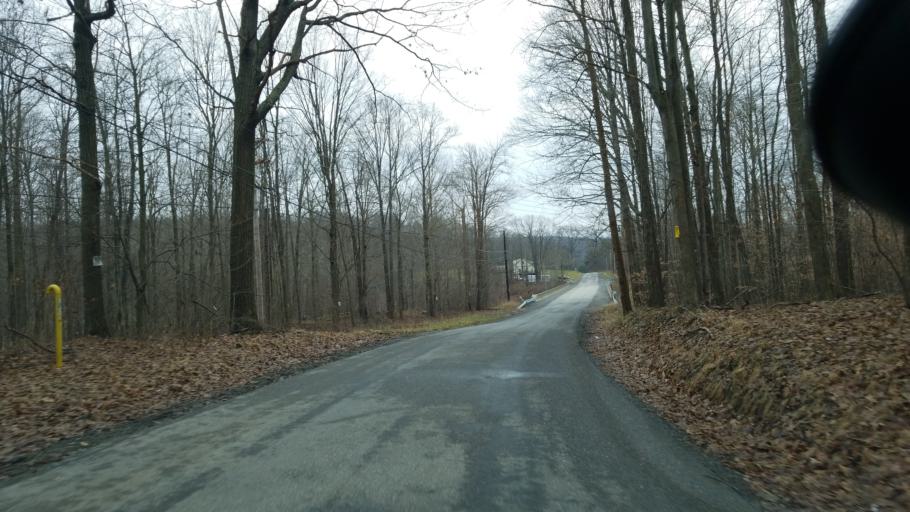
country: US
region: Pennsylvania
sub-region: Clearfield County
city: Treasure Lake
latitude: 41.1257
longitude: -78.6880
